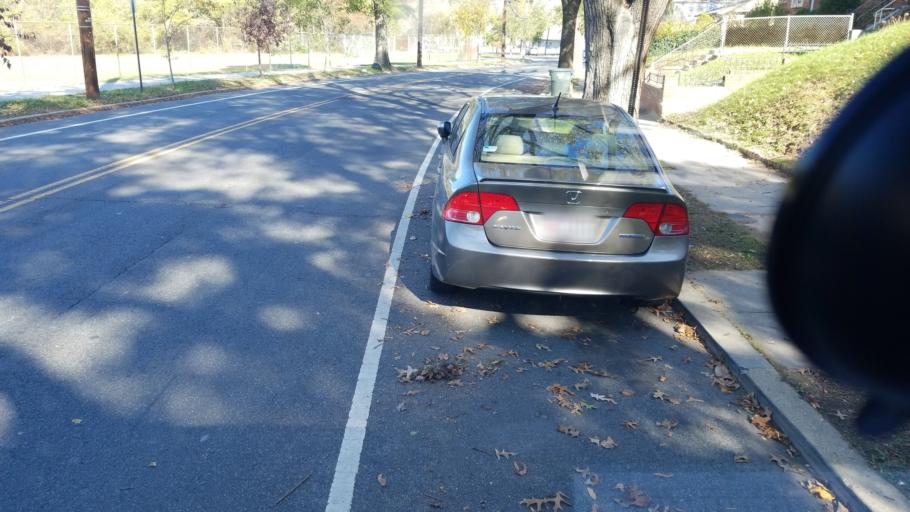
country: US
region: Maryland
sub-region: Prince George's County
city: Fairmount Heights
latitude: 38.8969
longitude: -76.9330
